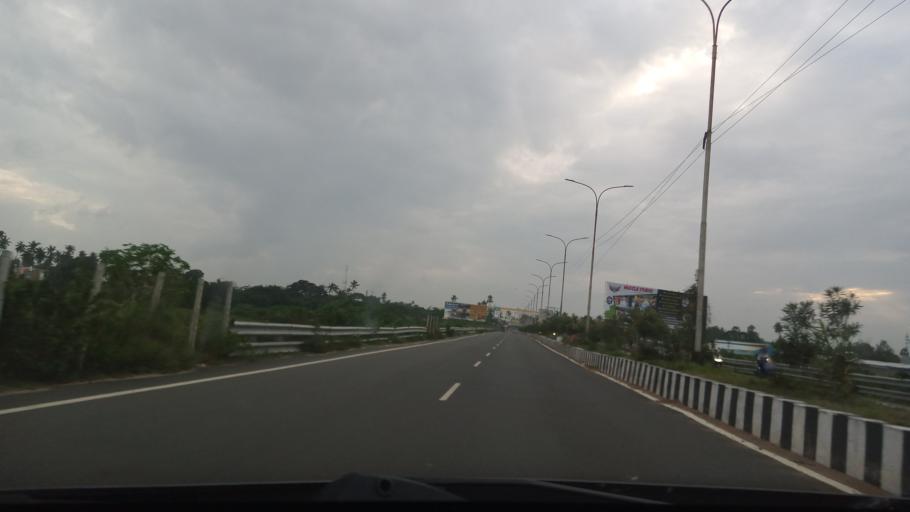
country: IN
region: Pondicherry
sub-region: Puducherry
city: Puducherry
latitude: 11.9623
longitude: 79.8322
